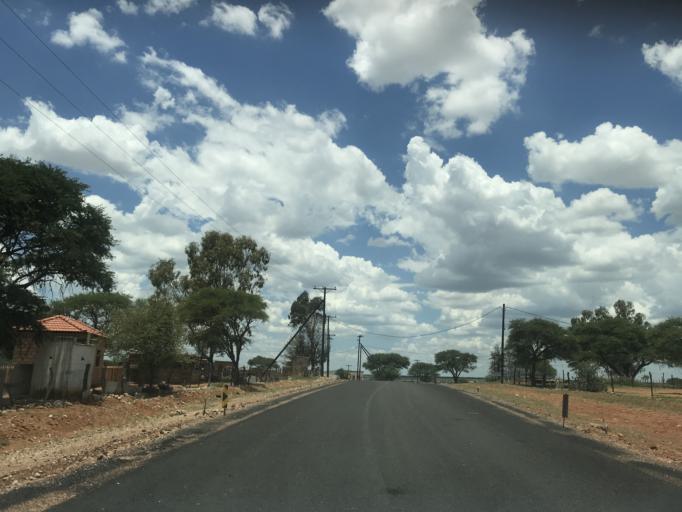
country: BW
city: Mabuli
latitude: -25.7903
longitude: 24.9010
